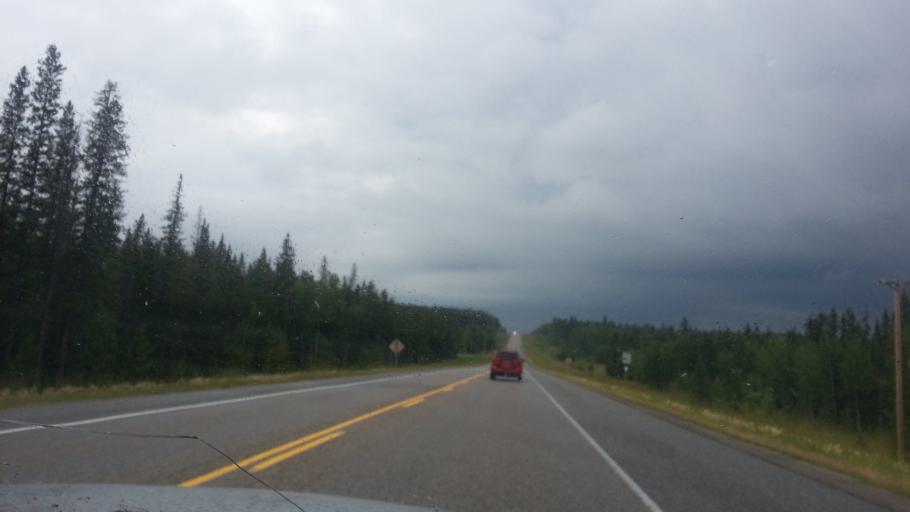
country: CA
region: Alberta
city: Cochrane
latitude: 50.9232
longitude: -114.5602
